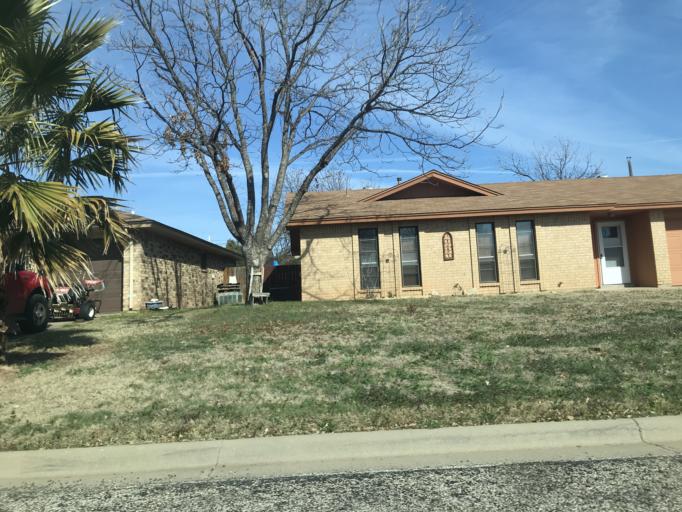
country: US
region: Texas
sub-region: Tom Green County
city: San Angelo
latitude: 31.4385
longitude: -100.4858
